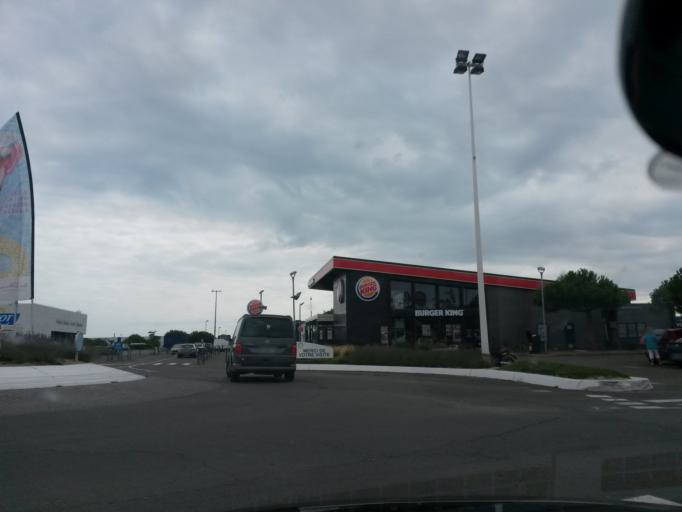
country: FR
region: Pays de la Loire
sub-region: Departement de la Vendee
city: Les Sables-d'Olonne
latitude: 46.5142
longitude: -1.7787
